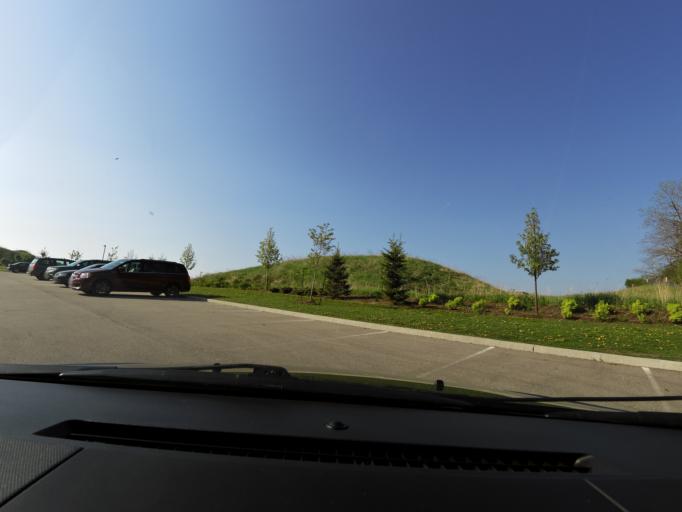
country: CA
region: Ontario
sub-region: Wellington County
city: Guelph
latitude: 43.5249
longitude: -80.2347
